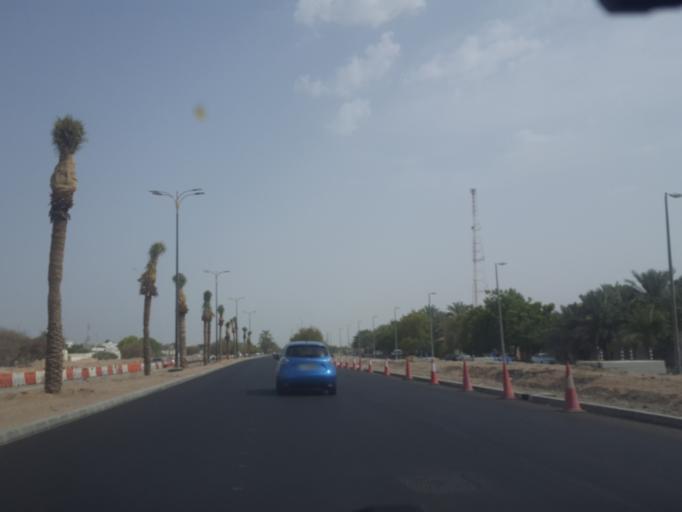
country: AE
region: Abu Dhabi
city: Al Ain
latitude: 24.2025
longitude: 55.7838
